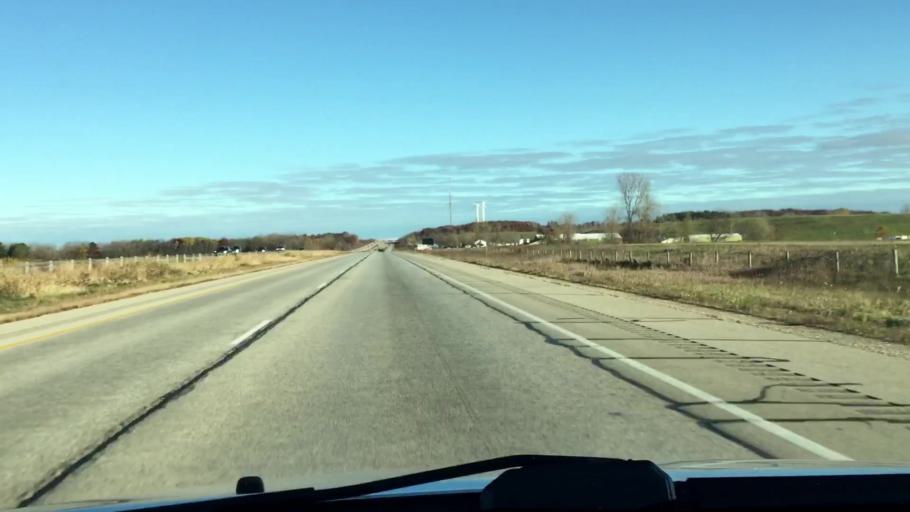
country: US
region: Wisconsin
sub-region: Dodge County
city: Lomira
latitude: 43.6402
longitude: -88.4412
